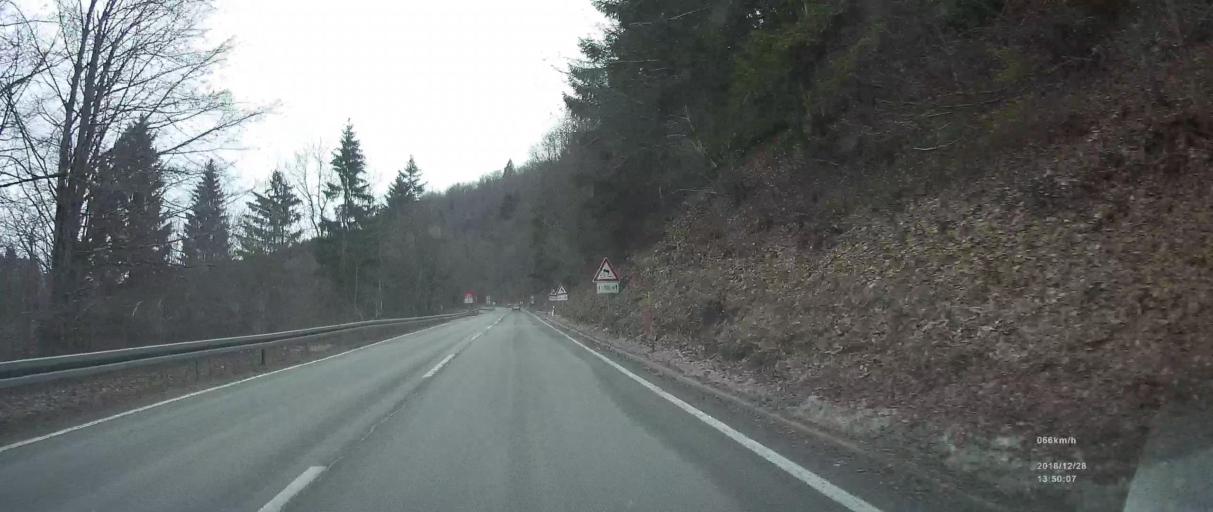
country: HR
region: Primorsko-Goranska
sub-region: Grad Delnice
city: Delnice
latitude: 45.3959
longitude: 14.8265
